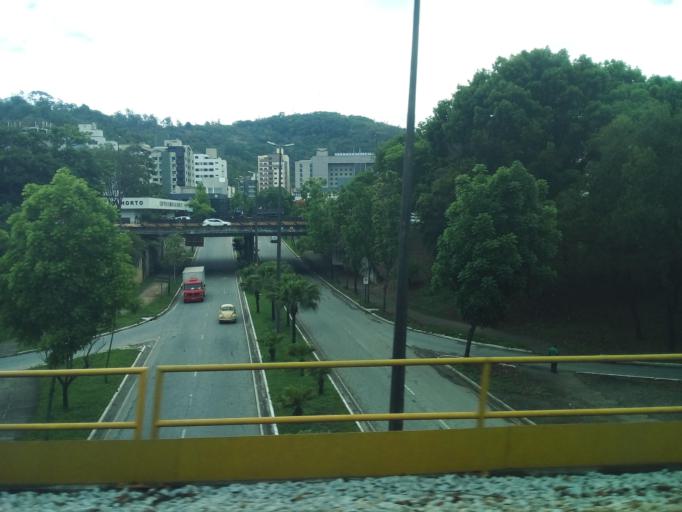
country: BR
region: Minas Gerais
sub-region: Ipatinga
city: Ipatinga
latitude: -19.5067
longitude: -42.5690
